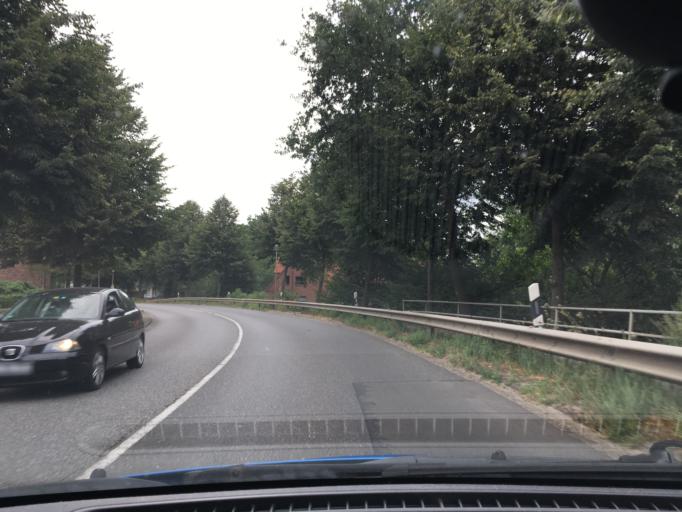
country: DE
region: Lower Saxony
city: Neu Wulmstorf
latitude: 53.4485
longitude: 9.7571
